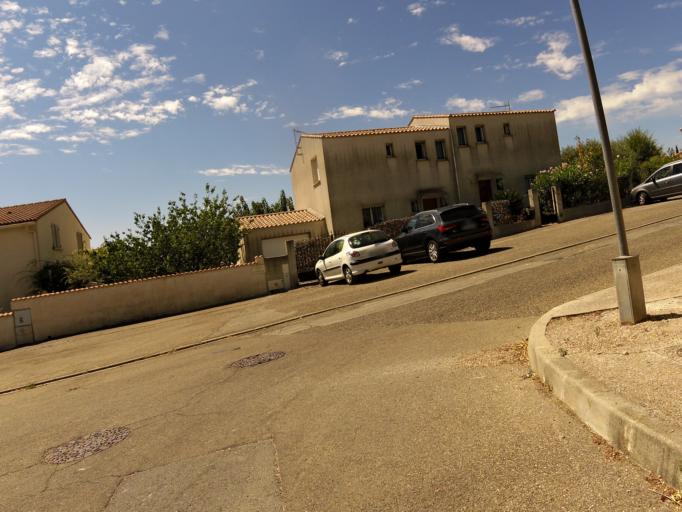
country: FR
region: Languedoc-Roussillon
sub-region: Departement du Gard
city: Vergeze
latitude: 43.7427
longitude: 4.2288
